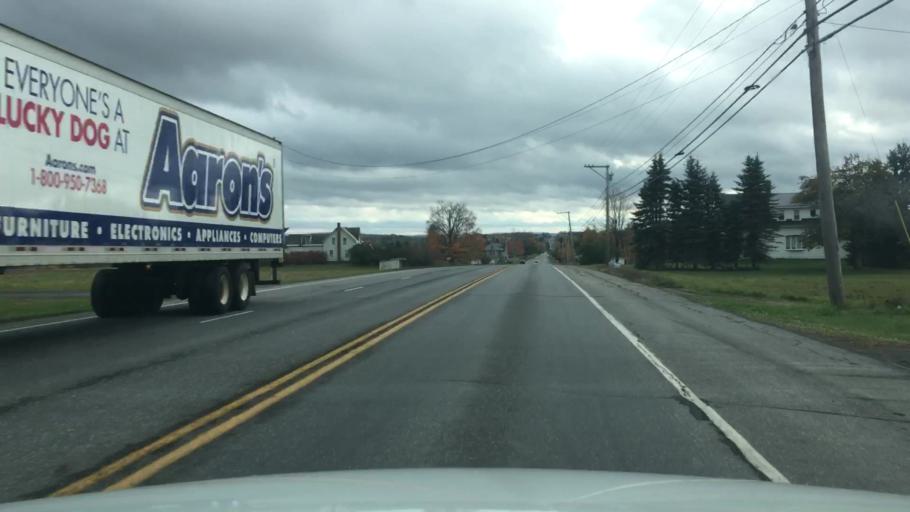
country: US
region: Maine
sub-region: Aroostook County
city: Houlton
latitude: 46.2213
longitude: -67.8411
